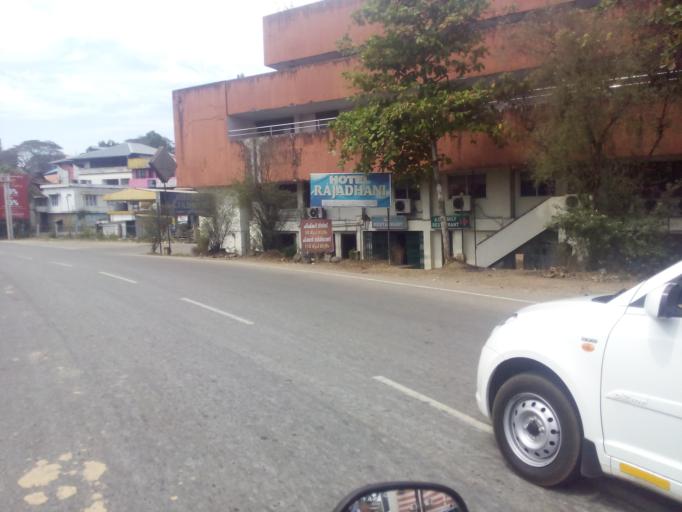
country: IN
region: Kerala
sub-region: Kottayam
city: Lalam
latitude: 9.7124
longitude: 76.6855
